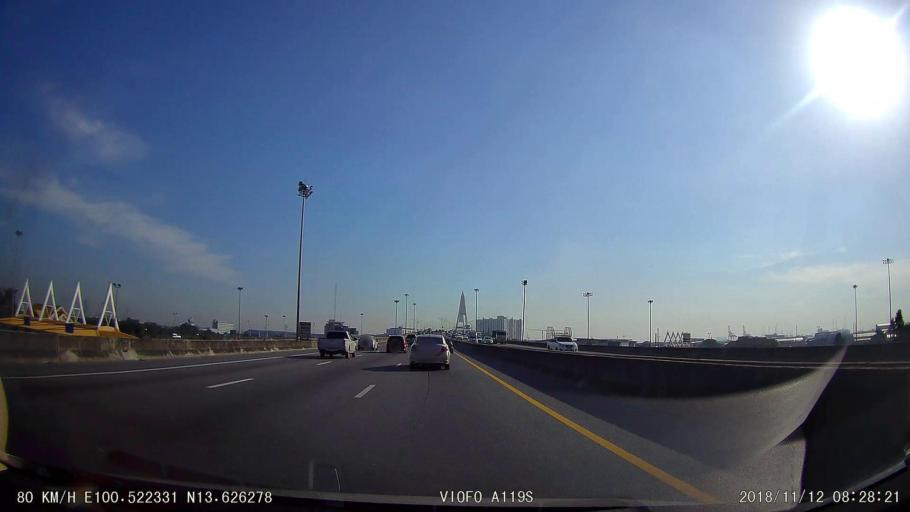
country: TH
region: Bangkok
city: Thung Khru
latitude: 13.6263
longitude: 100.5224
